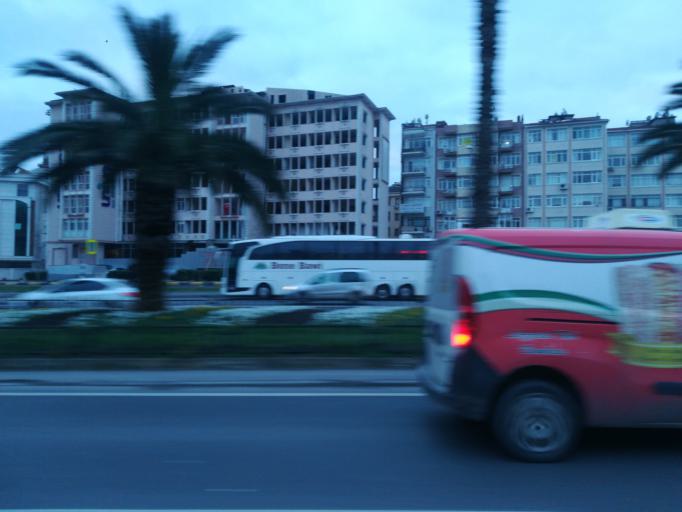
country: TR
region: Istanbul
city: Istanbul
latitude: 41.0130
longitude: 28.9462
